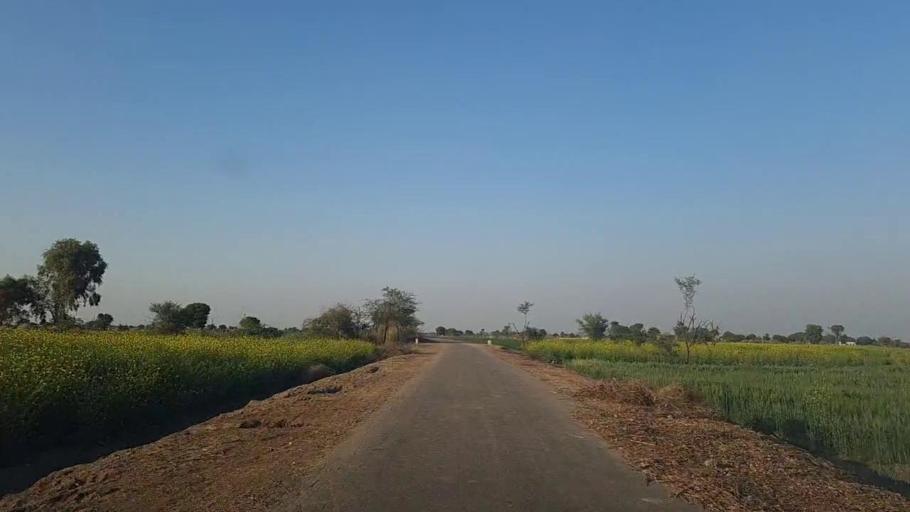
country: PK
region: Sindh
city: Jam Sahib
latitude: 26.3447
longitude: 68.6733
